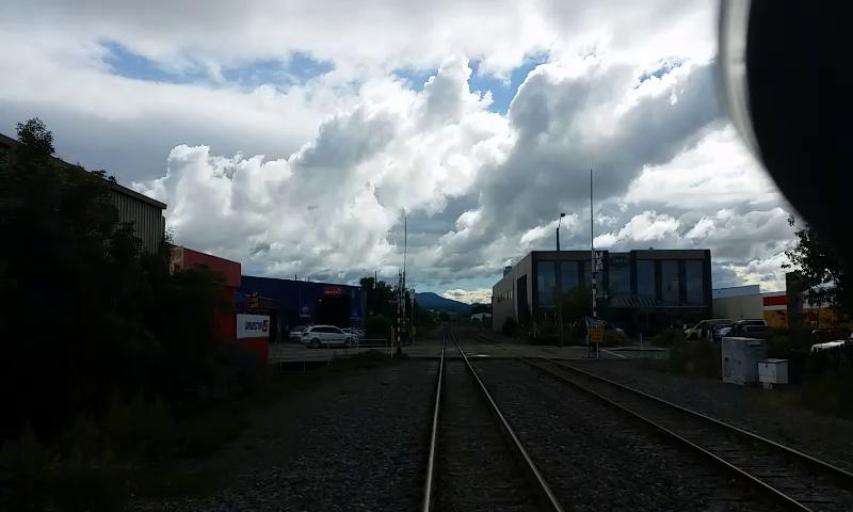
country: NZ
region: Canterbury
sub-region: Waimakariri District
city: Woodend
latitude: -43.3034
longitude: 172.5983
